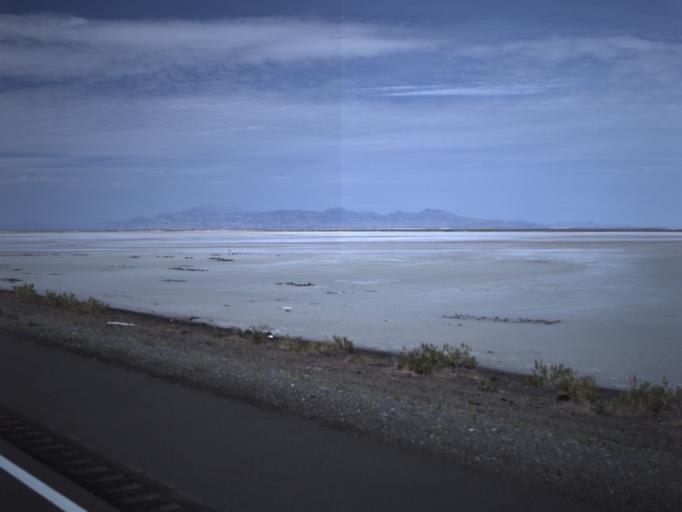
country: US
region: Utah
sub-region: Tooele County
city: Wendover
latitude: 40.7300
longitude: -113.4247
